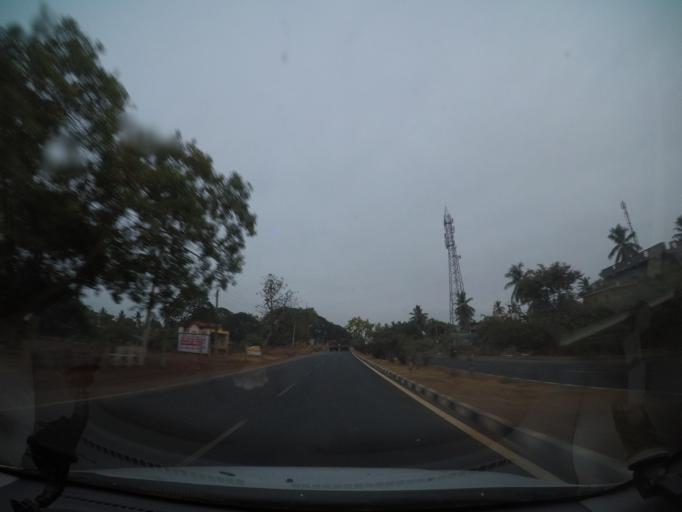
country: IN
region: Andhra Pradesh
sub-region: West Godavari
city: Eluru
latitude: 16.8048
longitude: 81.3036
